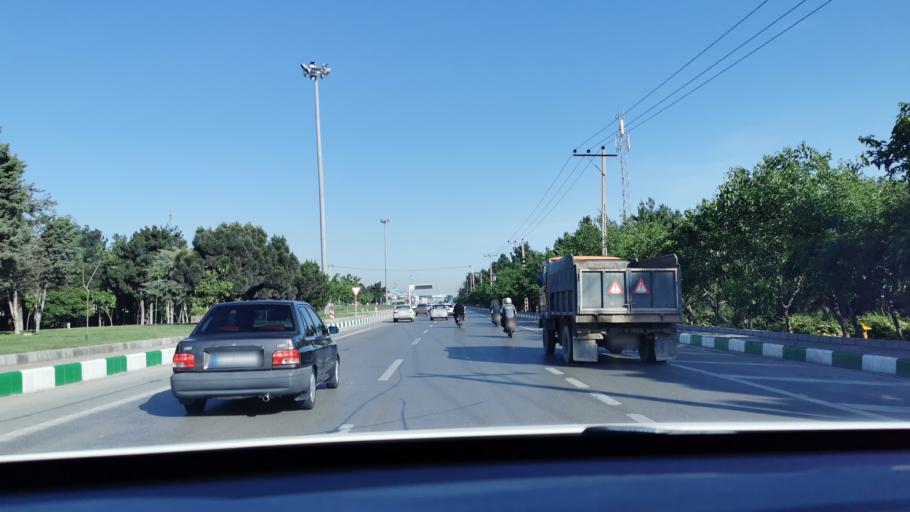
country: IR
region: Razavi Khorasan
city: Mashhad
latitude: 36.2513
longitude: 59.6085
